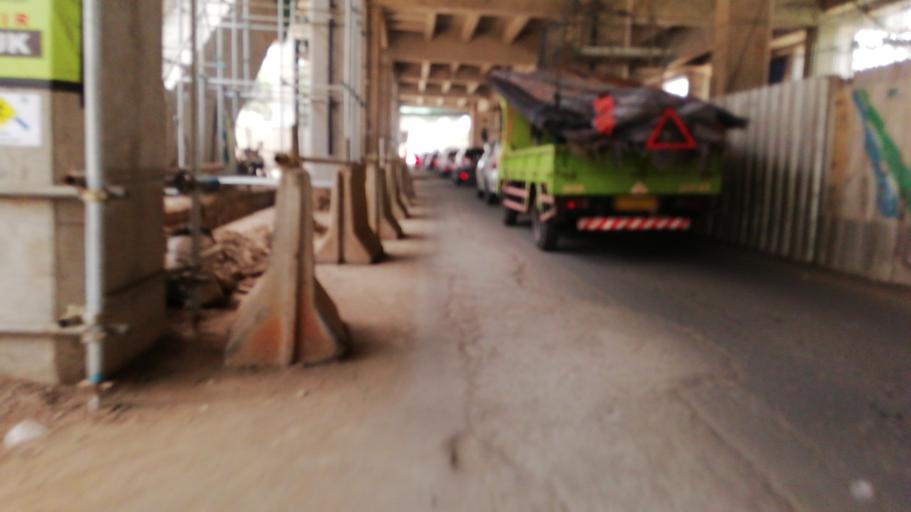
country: ID
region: Banten
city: South Tangerang
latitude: -6.2788
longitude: 106.7971
